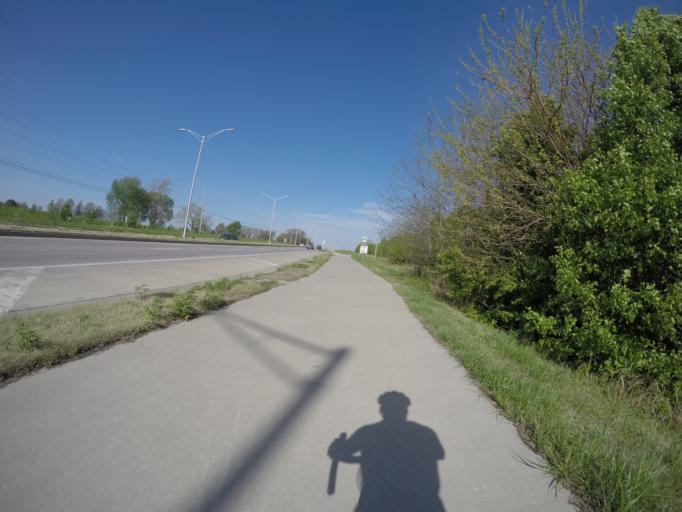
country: US
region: Missouri
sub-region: Cass County
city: Lake Winnebago
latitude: 38.8535
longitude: -94.3998
